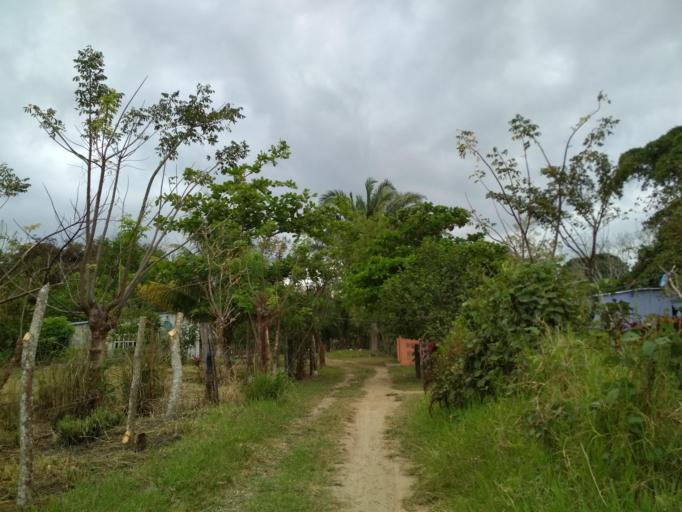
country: MX
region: Veracruz
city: El Tejar
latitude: 19.0637
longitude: -96.1529
